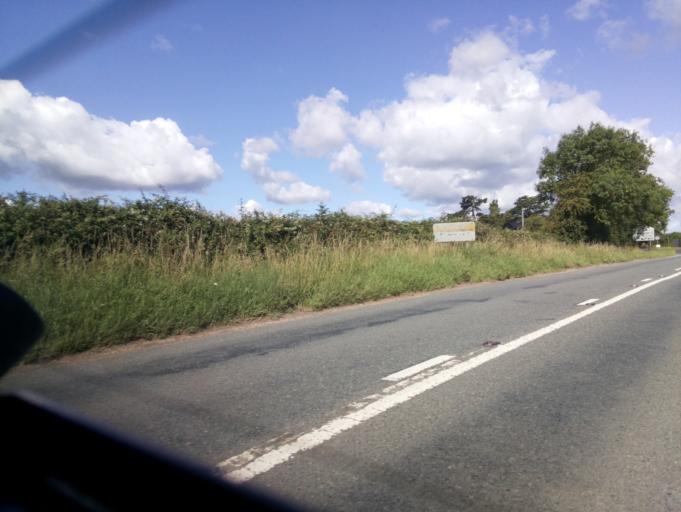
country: GB
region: England
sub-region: Gloucestershire
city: Newent
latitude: 51.9294
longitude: -2.3851
